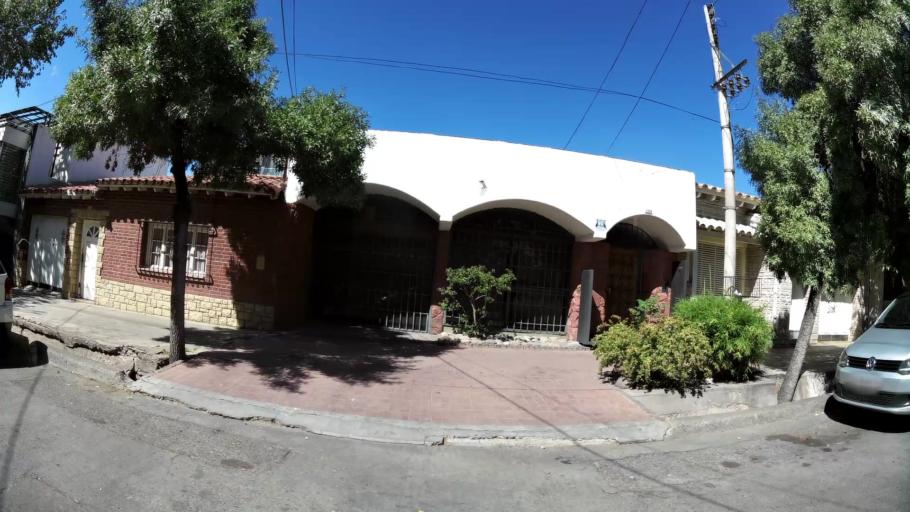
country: AR
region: Mendoza
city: Mendoza
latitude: -32.9005
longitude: -68.8592
